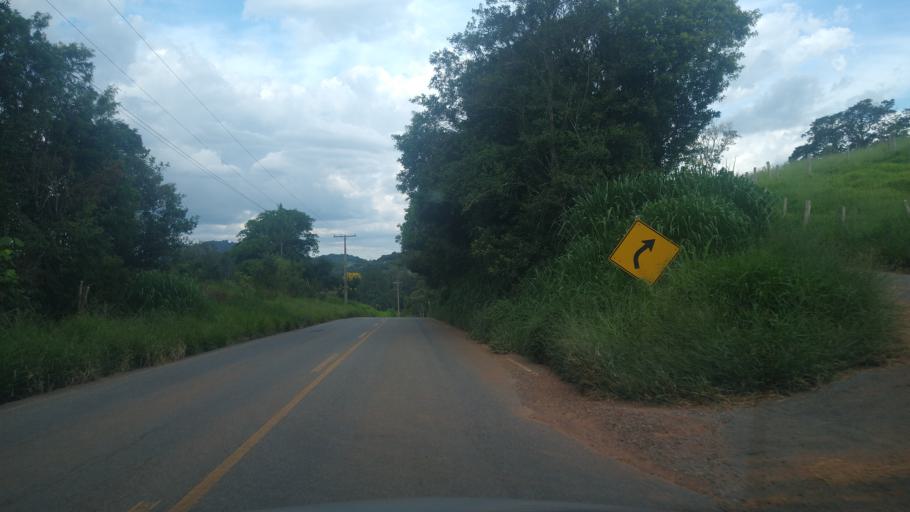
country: BR
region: Minas Gerais
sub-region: Extrema
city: Extrema
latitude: -22.8071
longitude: -46.3063
